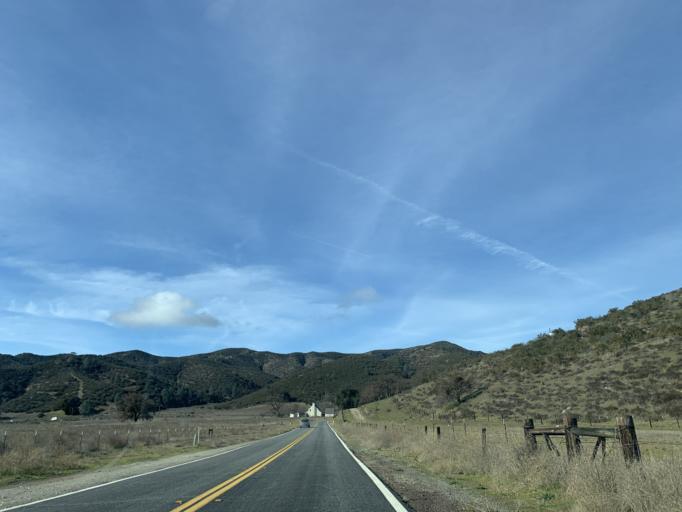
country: US
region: California
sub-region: Monterey County
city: Soledad
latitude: 36.5169
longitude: -121.1310
